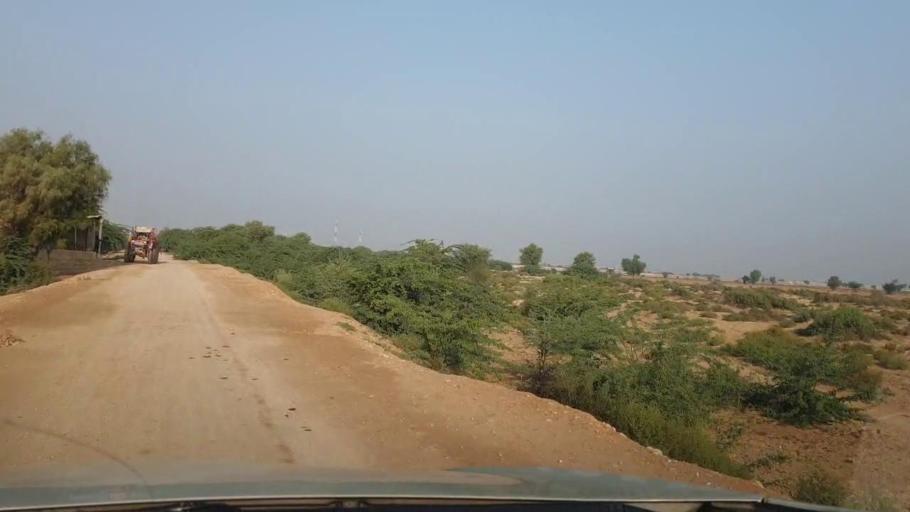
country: PK
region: Sindh
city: Sehwan
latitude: 26.3363
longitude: 67.7298
